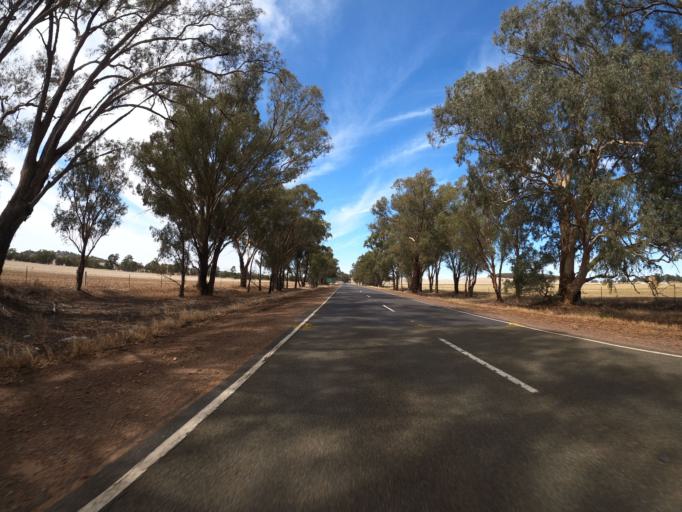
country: AU
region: Victoria
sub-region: Benalla
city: Benalla
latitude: -36.3147
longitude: 145.9583
